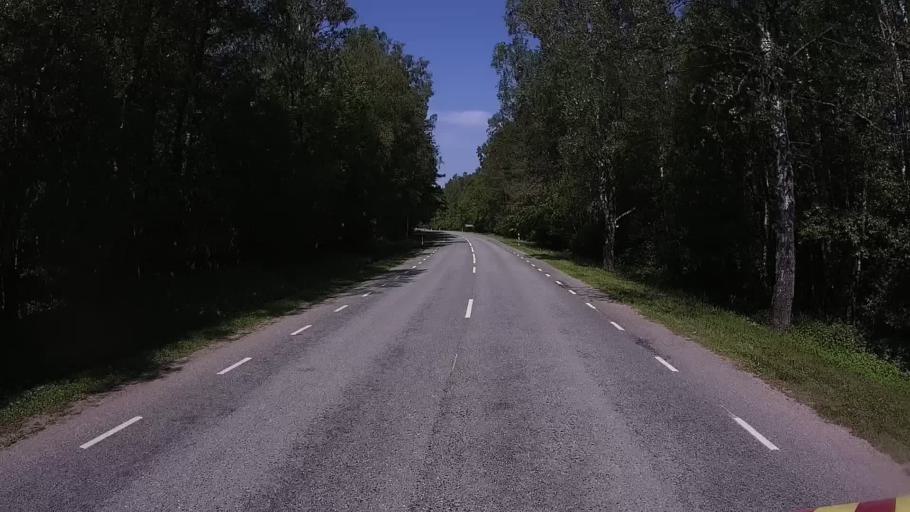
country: EE
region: Saare
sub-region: Kuressaare linn
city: Kuressaare
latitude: 58.3147
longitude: 22.2497
